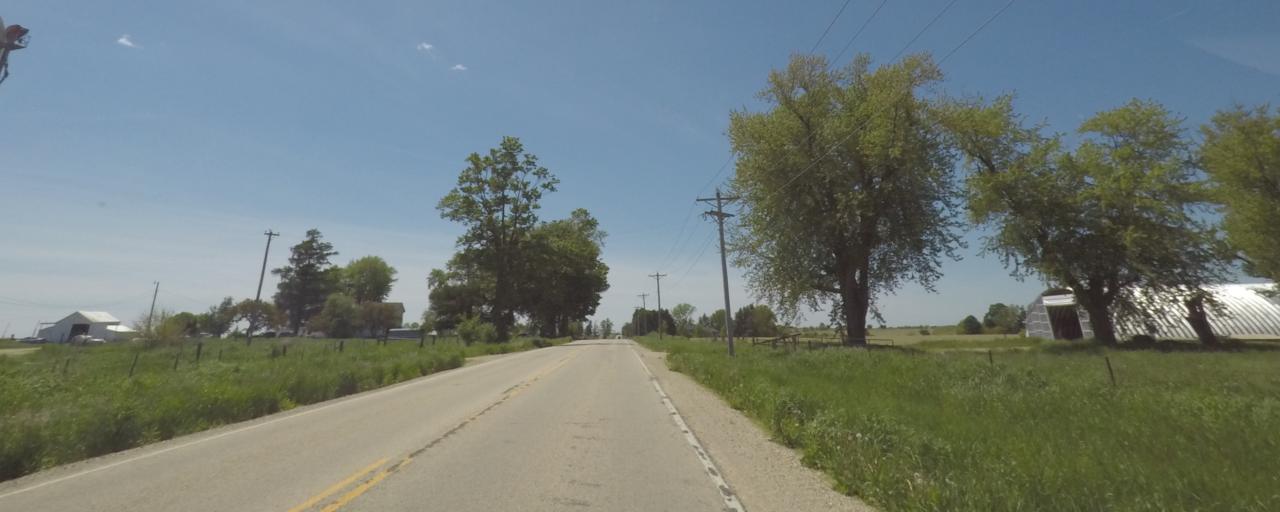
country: US
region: Wisconsin
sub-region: Rock County
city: Evansville
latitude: 42.7875
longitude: -89.3429
